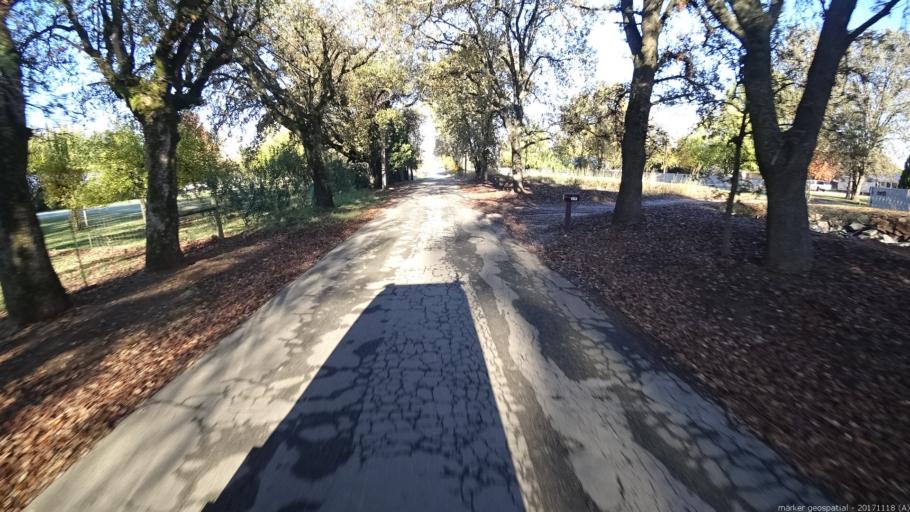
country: US
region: California
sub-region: Shasta County
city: Anderson
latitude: 40.4503
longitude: -122.2808
